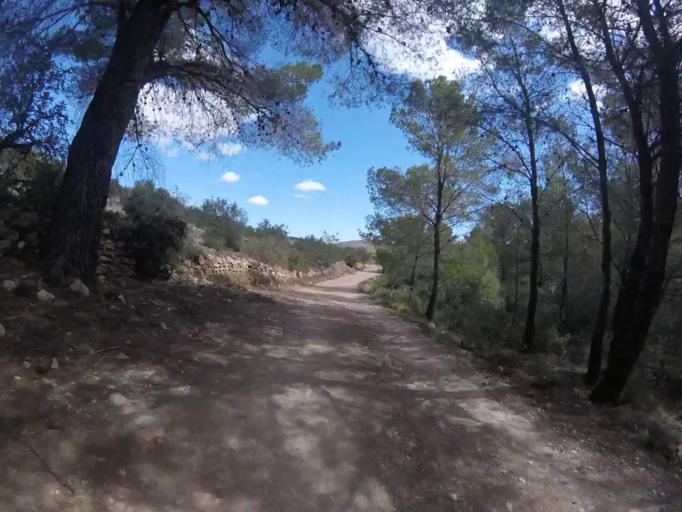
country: ES
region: Valencia
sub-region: Provincia de Castello
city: Santa Magdalena de Pulpis
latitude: 40.3137
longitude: 0.3295
